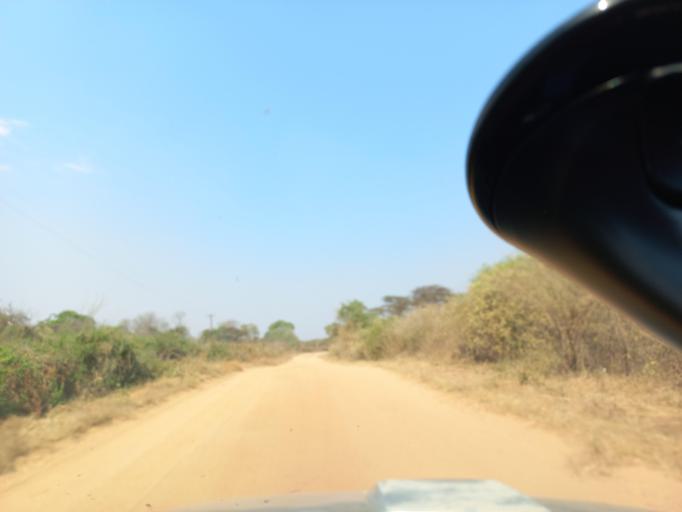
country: ZW
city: Chirundu
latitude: -15.9255
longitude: 28.8763
